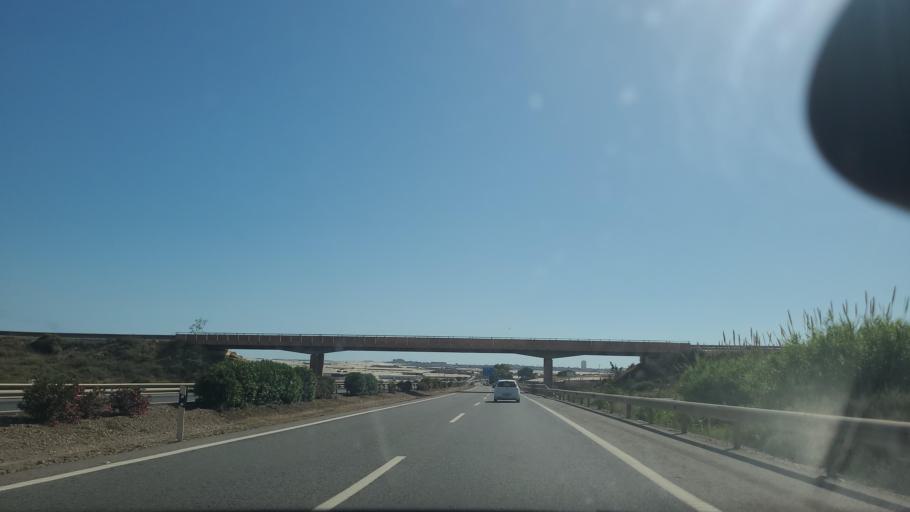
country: ES
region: Andalusia
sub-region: Provincia de Almeria
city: El Ejido
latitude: 36.7798
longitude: -2.7610
